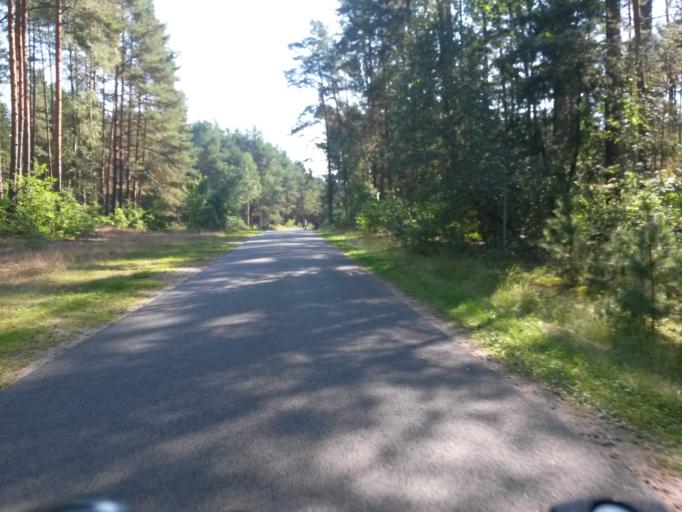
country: DE
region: Brandenburg
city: Templin
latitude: 53.0485
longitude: 13.4779
